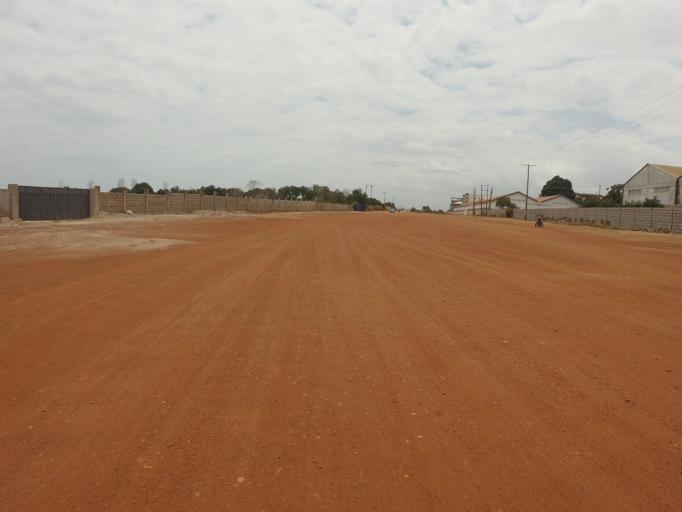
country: GH
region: Greater Accra
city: Medina Estates
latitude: 5.6346
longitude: -0.1293
